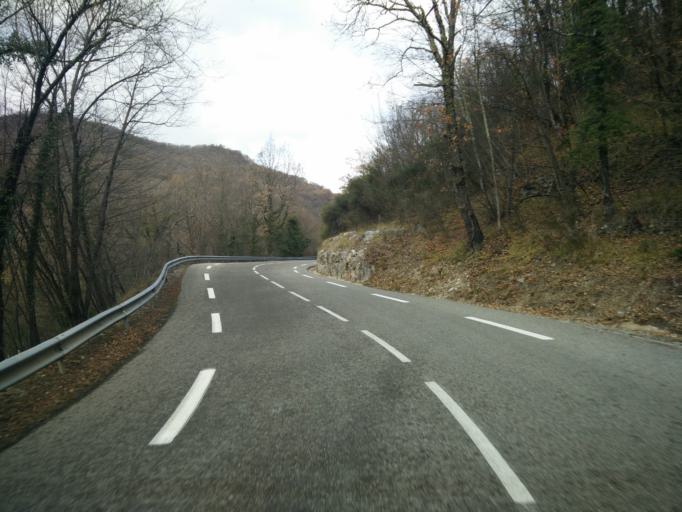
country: FR
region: Provence-Alpes-Cote d'Azur
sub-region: Departement des Alpes-Maritimes
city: Tourrettes-sur-Loup
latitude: 43.7669
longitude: 6.9870
